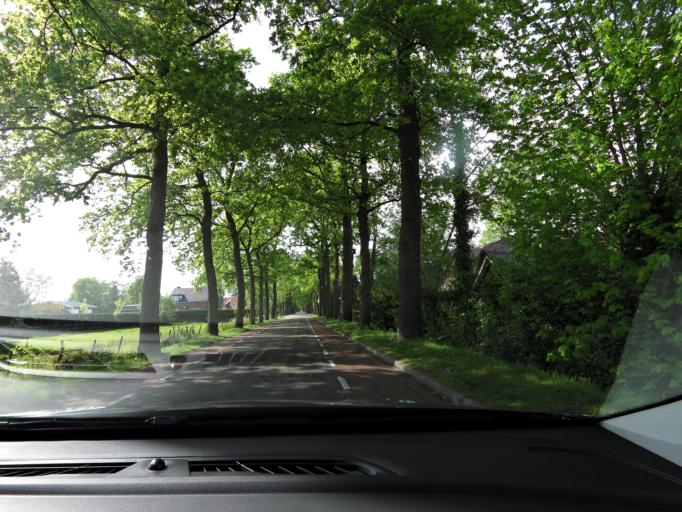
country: NL
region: Utrecht
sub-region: Gemeente Utrechtse Heuvelrug
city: Leersum
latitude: 52.0060
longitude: 5.4288
